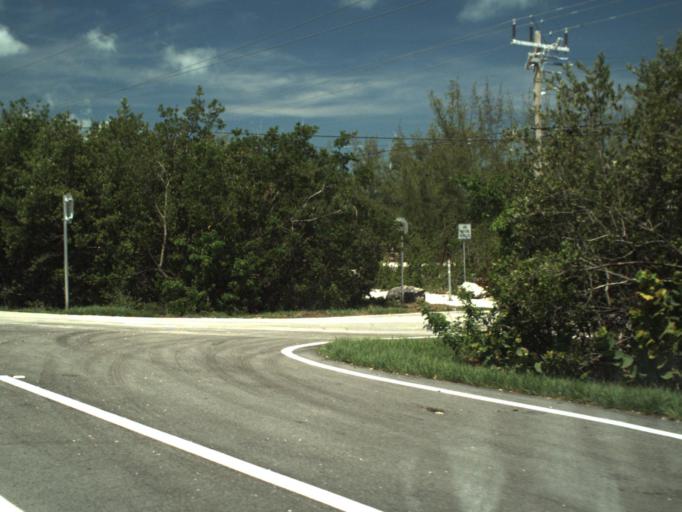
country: US
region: Florida
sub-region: Monroe County
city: Marathon
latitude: 24.7490
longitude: -80.9767
